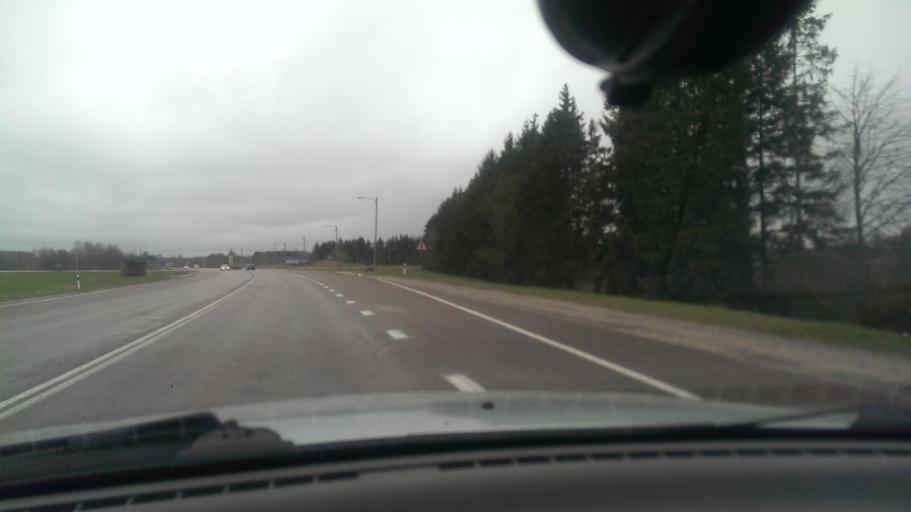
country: EE
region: Tartu
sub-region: Tartu linn
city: Tartu
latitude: 58.3628
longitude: 26.8897
